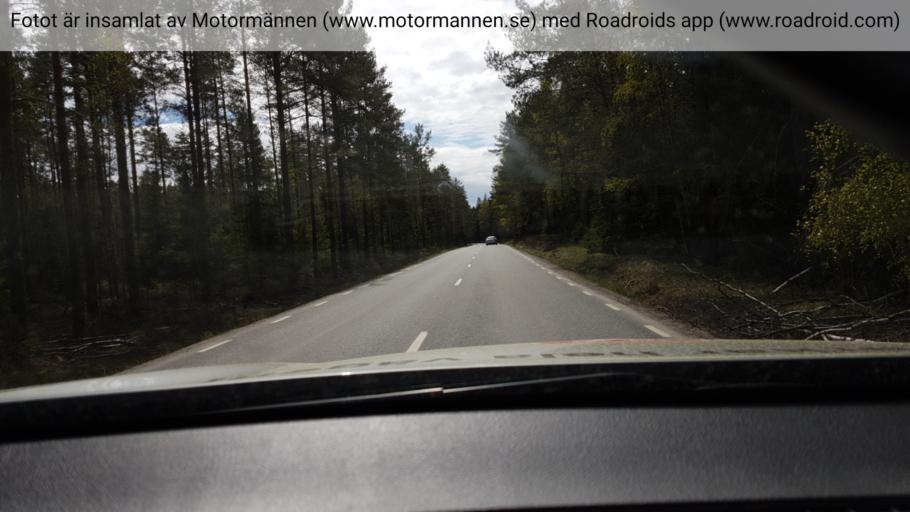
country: SE
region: Stockholm
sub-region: Haninge Kommun
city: Haninge
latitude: 59.1611
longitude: 18.1818
